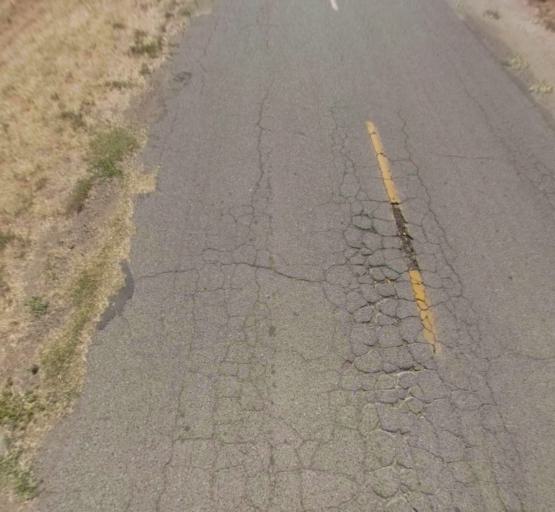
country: US
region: California
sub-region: Madera County
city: Chowchilla
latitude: 37.0909
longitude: -120.2643
